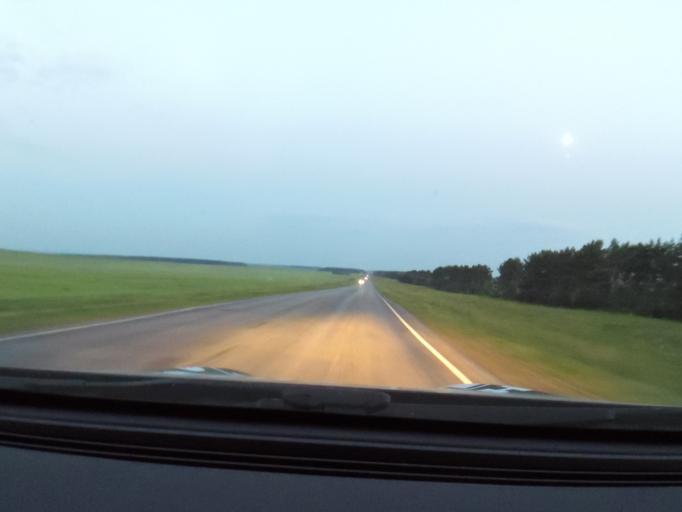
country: RU
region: Bashkortostan
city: Duvan
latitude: 56.1109
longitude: 58.0531
